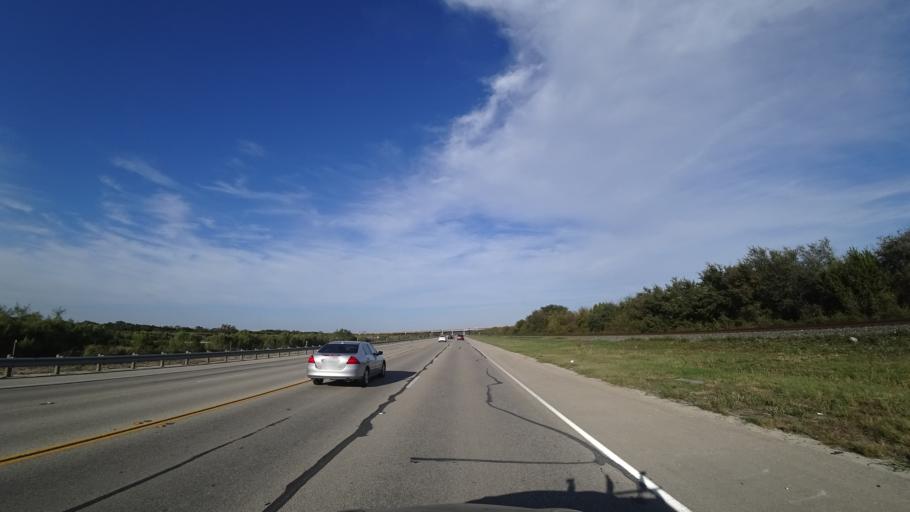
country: US
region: Texas
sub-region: Travis County
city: Wells Branch
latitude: 30.4686
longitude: -97.7111
